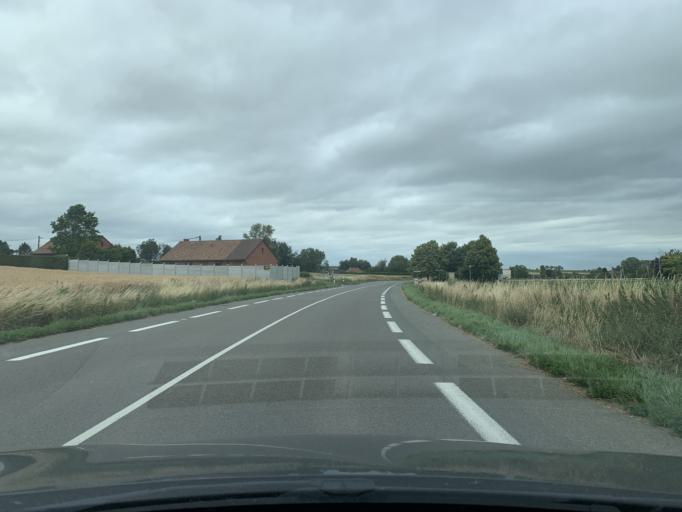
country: FR
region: Nord-Pas-de-Calais
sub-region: Departement du Nord
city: Neuville-Saint-Remy
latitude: 50.2196
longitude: 3.2200
